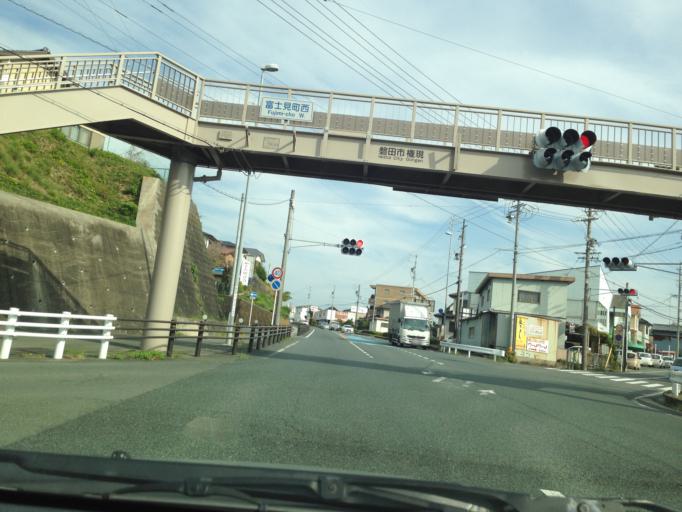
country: JP
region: Shizuoka
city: Iwata
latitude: 34.7265
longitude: 137.8651
